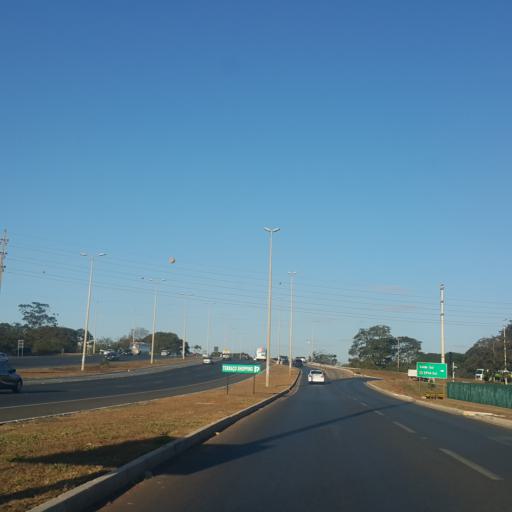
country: BR
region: Federal District
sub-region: Brasilia
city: Brasilia
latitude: -15.8101
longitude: -47.9510
